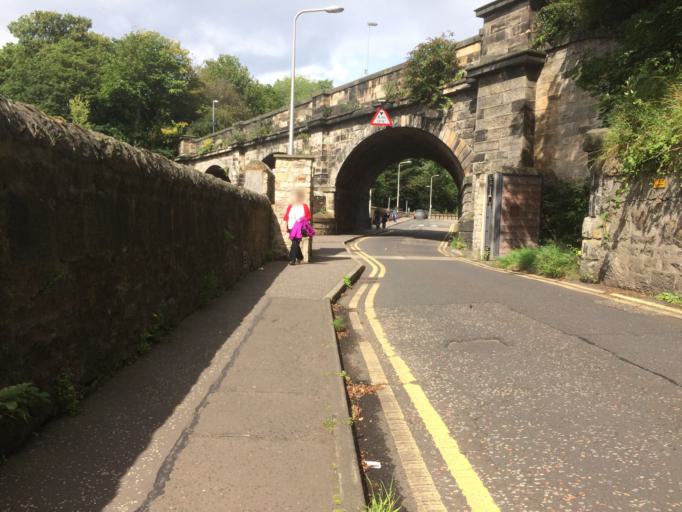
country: GB
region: Scotland
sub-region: Edinburgh
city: Edinburgh
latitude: 55.9651
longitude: -3.1989
